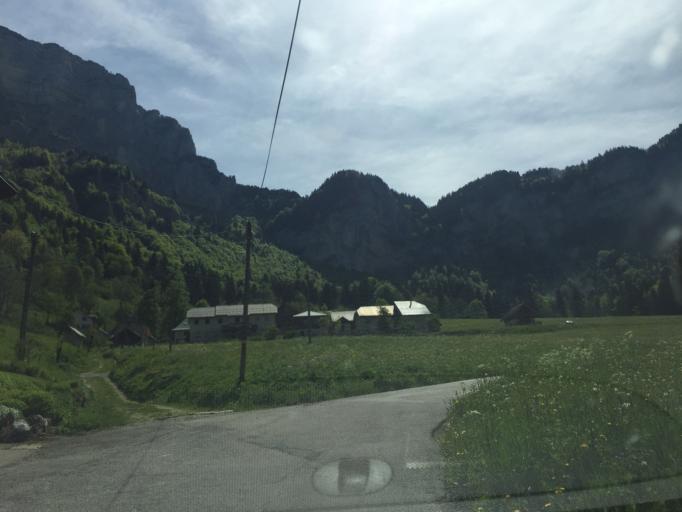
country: FR
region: Rhone-Alpes
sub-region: Departement de l'Isere
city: Barraux
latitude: 45.4441
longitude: 5.9046
